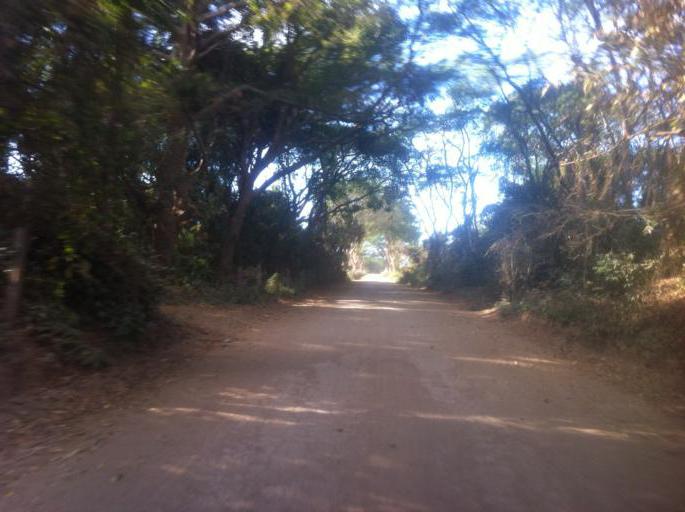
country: NI
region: Managua
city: Masachapa
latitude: 11.8377
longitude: -86.5201
